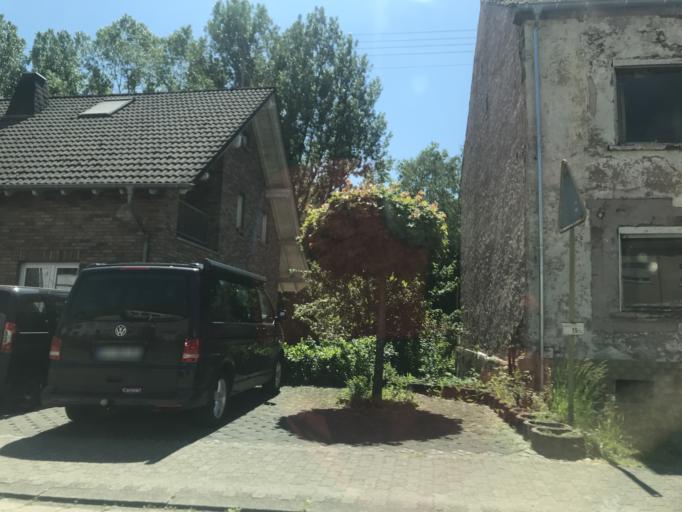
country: DE
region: Saarland
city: Losheim
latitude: 49.4503
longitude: 6.7623
